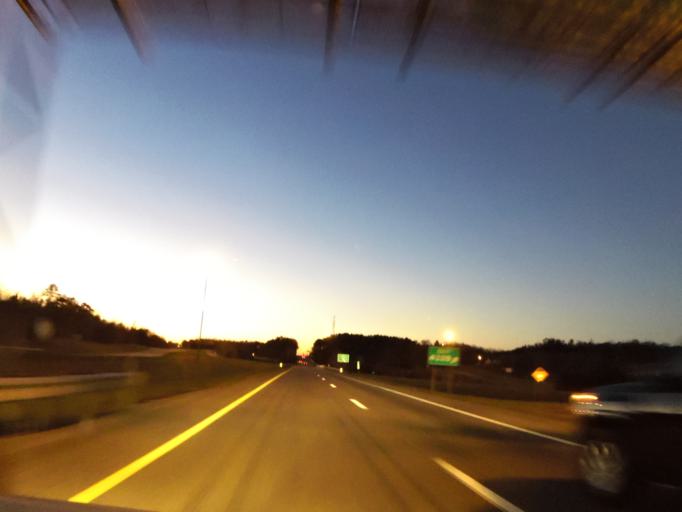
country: US
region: Tennessee
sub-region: Cocke County
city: Newport
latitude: 35.9686
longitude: -83.2502
